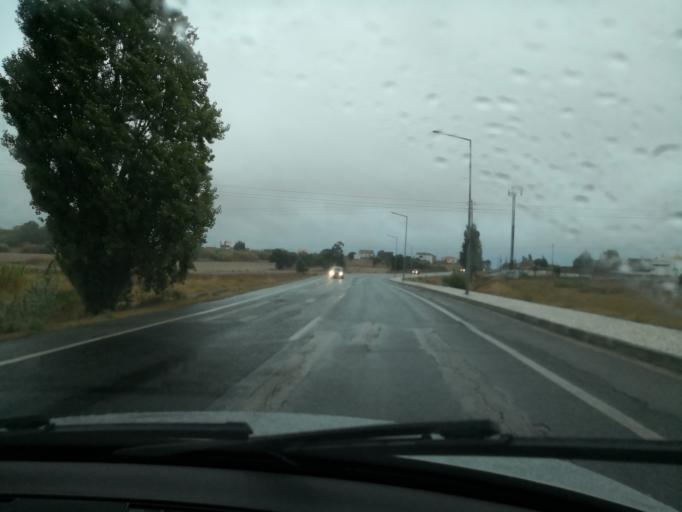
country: PT
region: Setubal
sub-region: Moita
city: Moita
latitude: 38.6467
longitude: -8.9836
